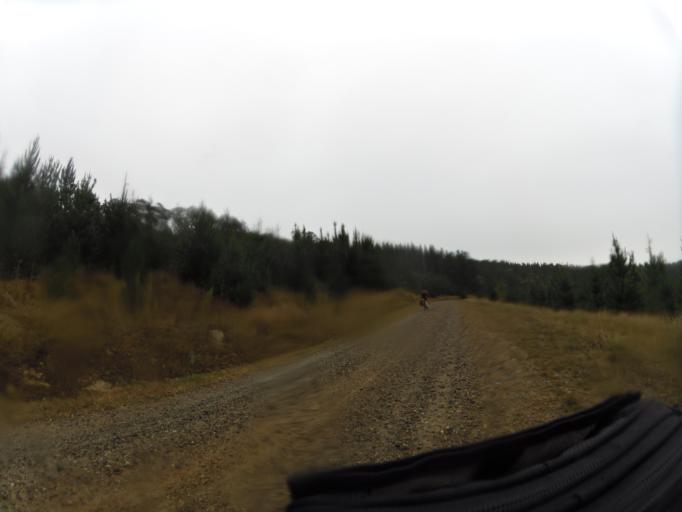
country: AU
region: New South Wales
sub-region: Greater Hume Shire
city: Holbrook
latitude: -36.2055
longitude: 147.5677
